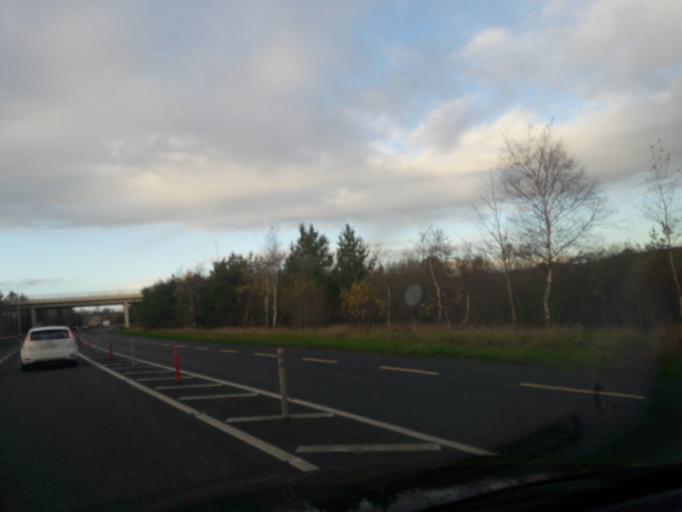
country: IE
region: Ulster
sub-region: County Monaghan
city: Carrickmacross
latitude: 53.9883
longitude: -6.7158
